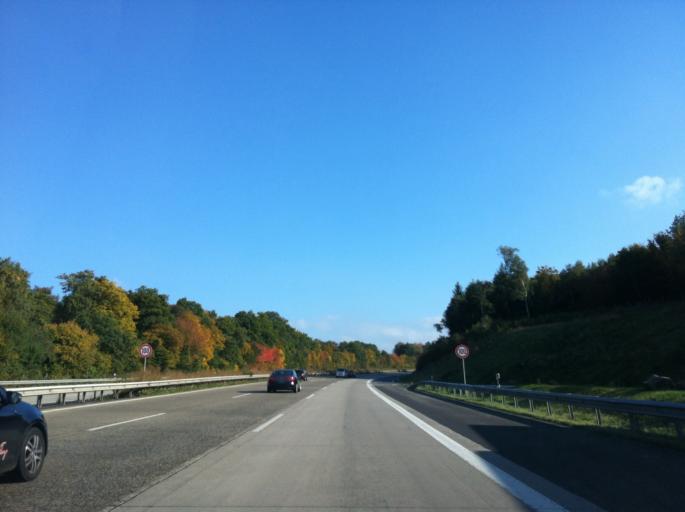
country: DE
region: Rheinland-Pfalz
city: Windhagen
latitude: 50.6278
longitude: 7.3849
